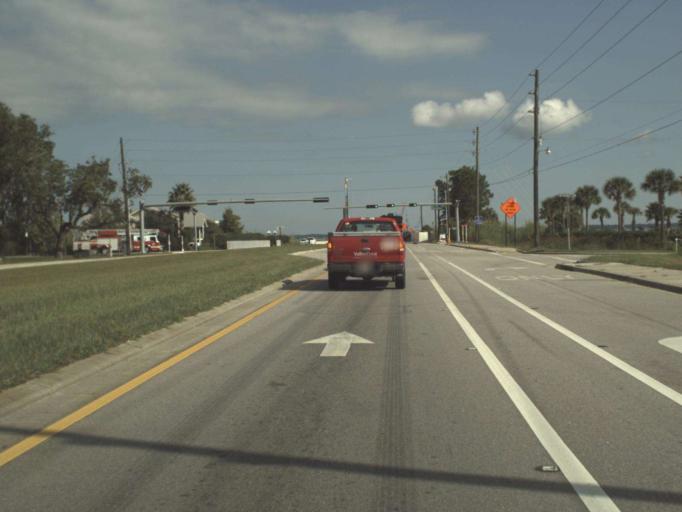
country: US
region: Florida
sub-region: Walton County
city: Seaside
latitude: 30.3865
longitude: -86.1749
